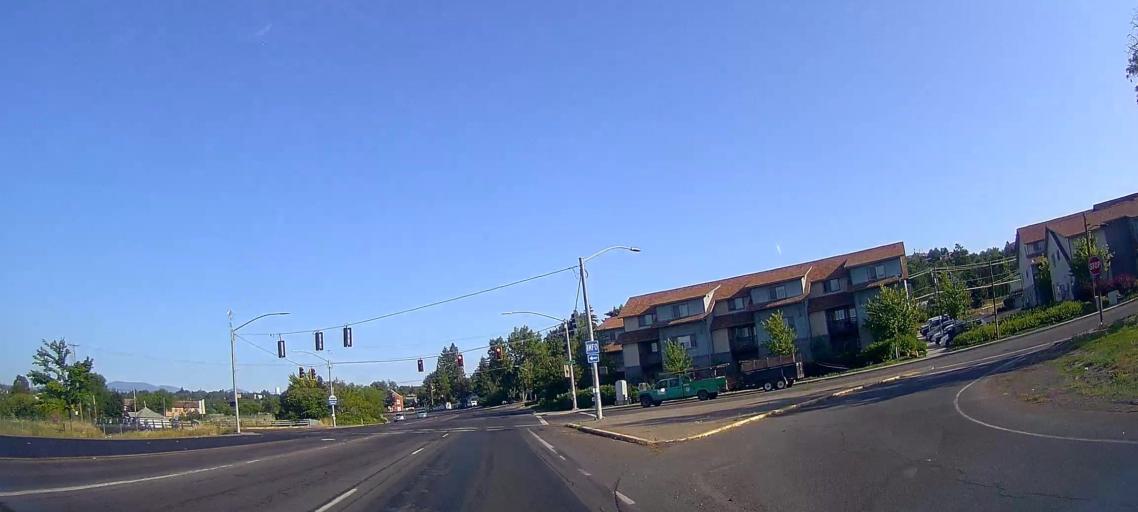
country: US
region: Oregon
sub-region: Klamath County
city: Klamath Falls
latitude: 42.2281
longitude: -121.7657
